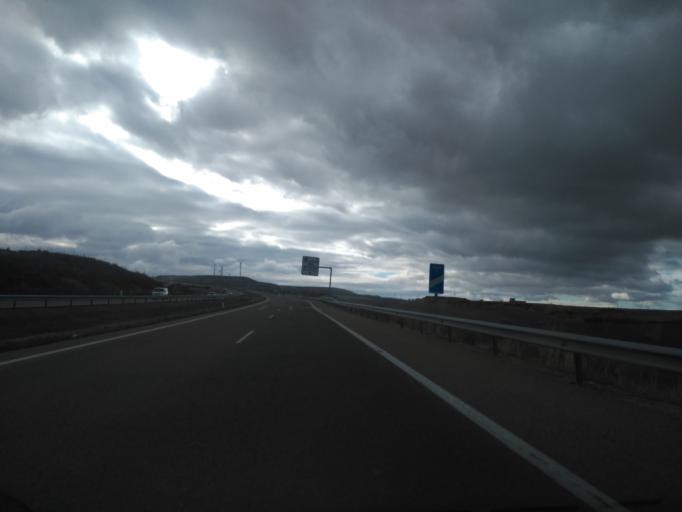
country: ES
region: Castille and Leon
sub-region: Provincia de Palencia
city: Monzon de Campos
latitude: 42.1249
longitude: -4.4790
